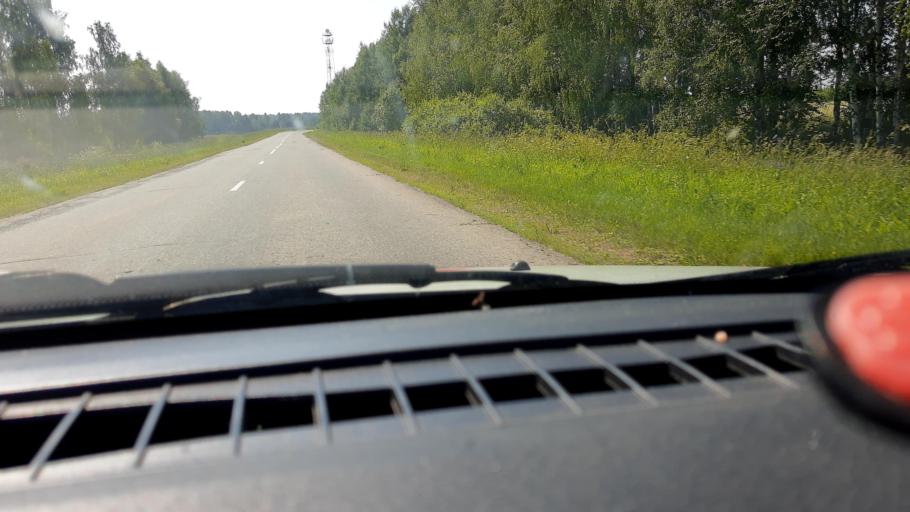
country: RU
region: Nizjnij Novgorod
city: Sharanga
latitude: 57.0612
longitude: 46.5452
